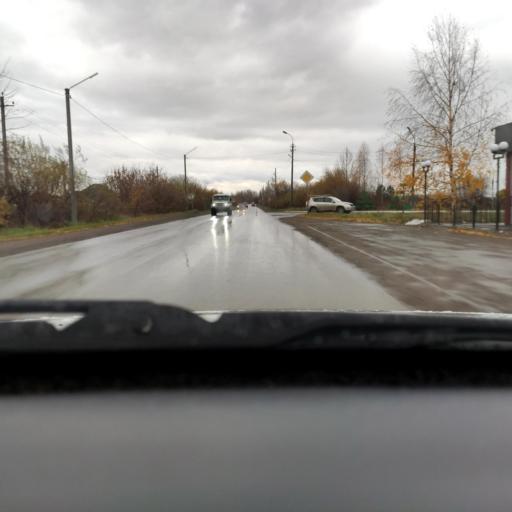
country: RU
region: Perm
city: Kondratovo
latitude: 57.9745
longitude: 56.1110
